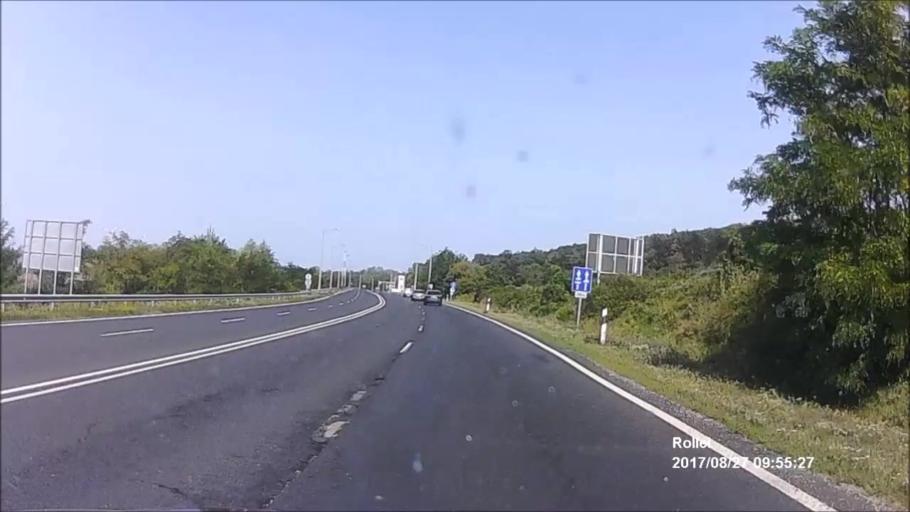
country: AT
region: Burgenland
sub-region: Eisenstadt-Umgebung
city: Klingenbach
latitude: 47.7323
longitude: 16.5545
